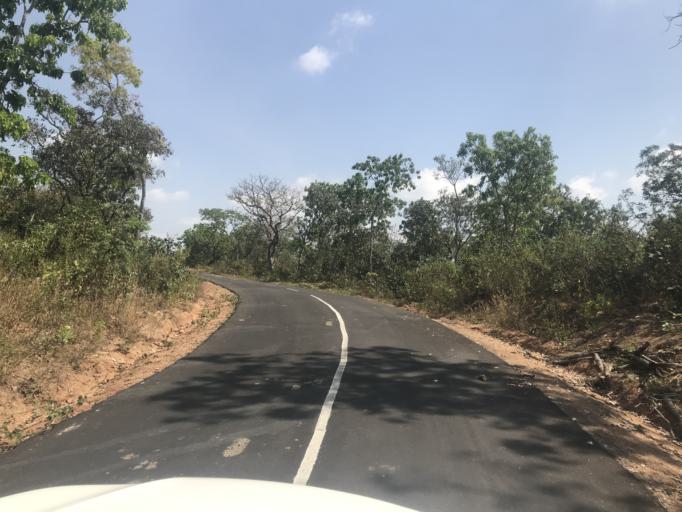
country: NG
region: Osun
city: Otan Ayegbaju
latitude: 7.8956
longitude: 4.8362
